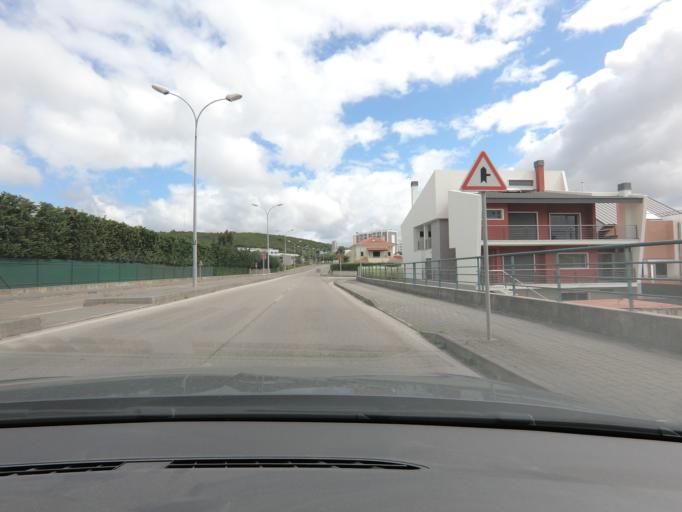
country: PT
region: Lisbon
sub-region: Oeiras
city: Carnaxide
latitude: 38.7305
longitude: -9.2343
